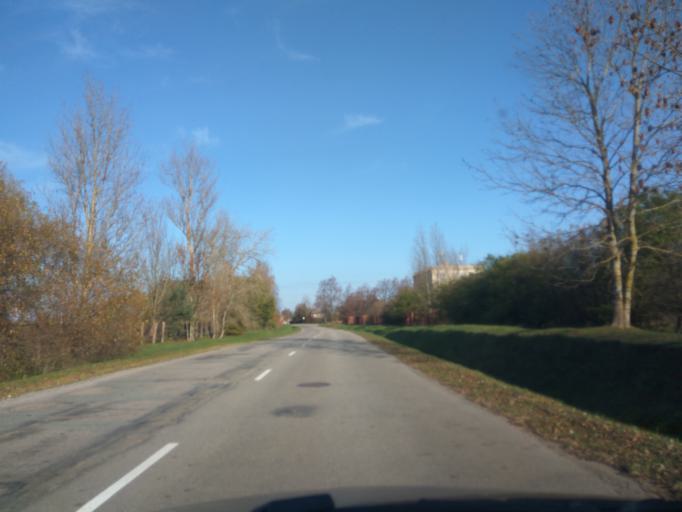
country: LV
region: Ventspils
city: Ventspils
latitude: 57.3692
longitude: 21.5661
